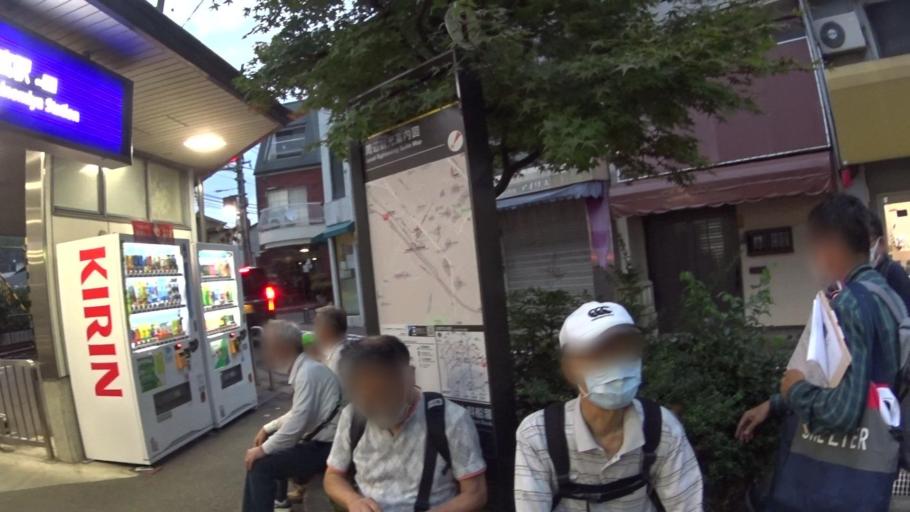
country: JP
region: Osaka
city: Kaizuka
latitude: 34.4410
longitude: 135.2735
